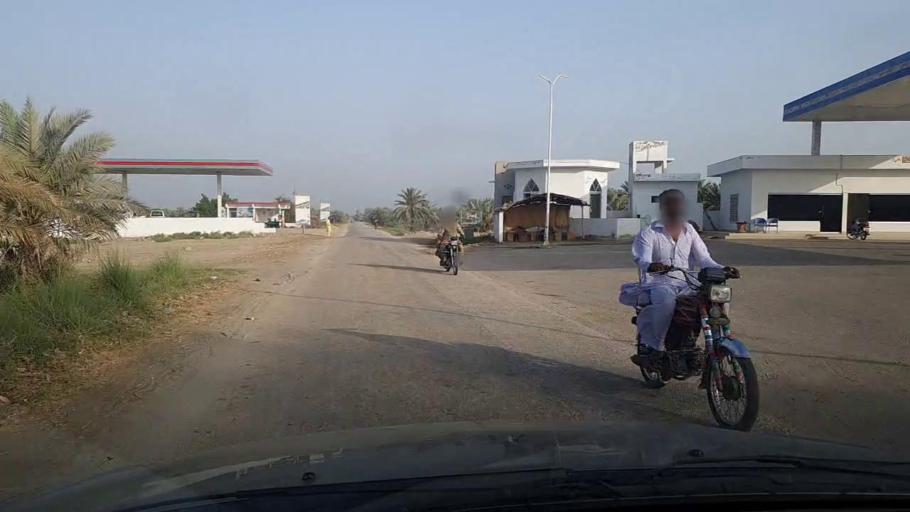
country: PK
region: Sindh
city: Khairpur
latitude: 27.5397
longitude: 68.7096
